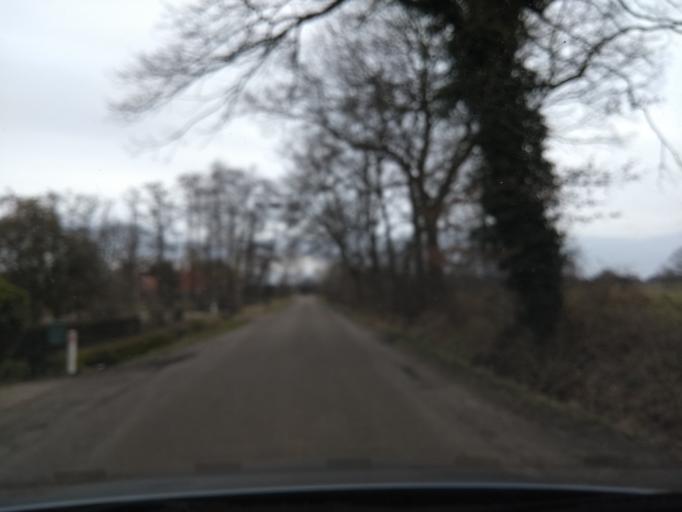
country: NL
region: Overijssel
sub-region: Gemeente Borne
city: Borne
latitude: 52.3511
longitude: 6.7359
